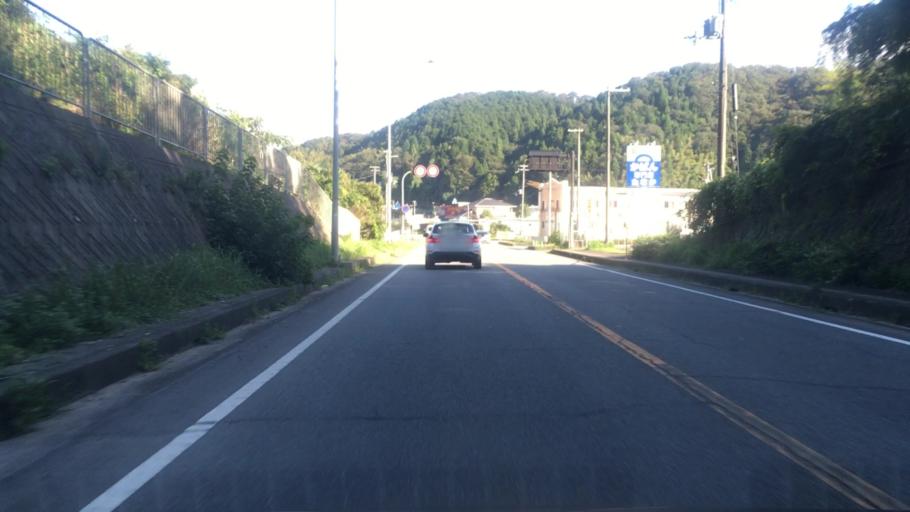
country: JP
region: Hyogo
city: Toyooka
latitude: 35.5558
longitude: 134.8328
